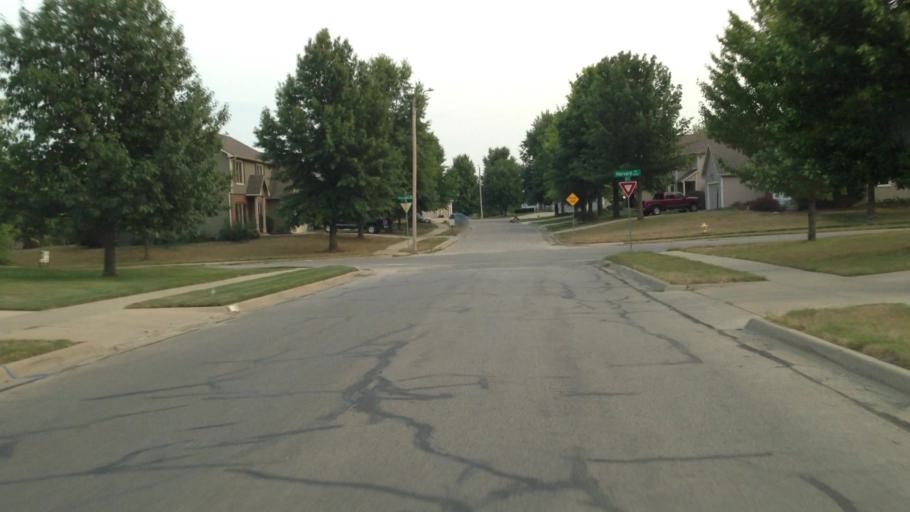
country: US
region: Kansas
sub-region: Douglas County
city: Lawrence
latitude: 38.9683
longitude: -95.3102
